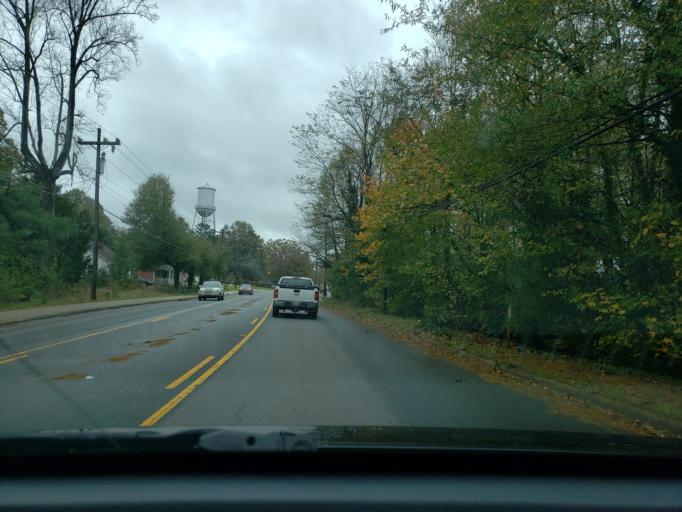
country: US
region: North Carolina
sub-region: Stokes County
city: Walnut Cove
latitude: 36.3065
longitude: -80.1421
